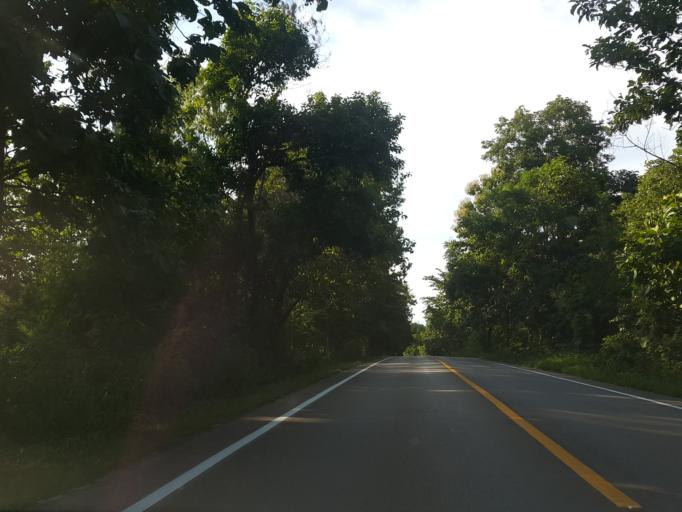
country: TH
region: Chiang Mai
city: Mae Taeng
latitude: 19.0805
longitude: 99.1036
